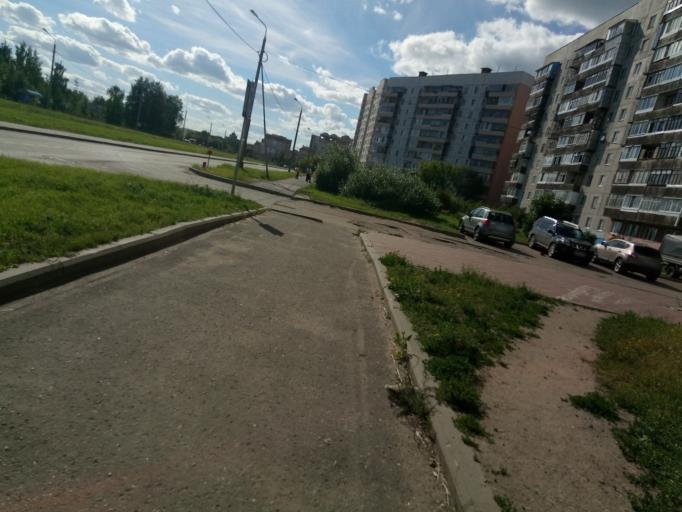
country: RU
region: Jaroslavl
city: Yaroslavl
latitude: 57.6376
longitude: 39.9577
